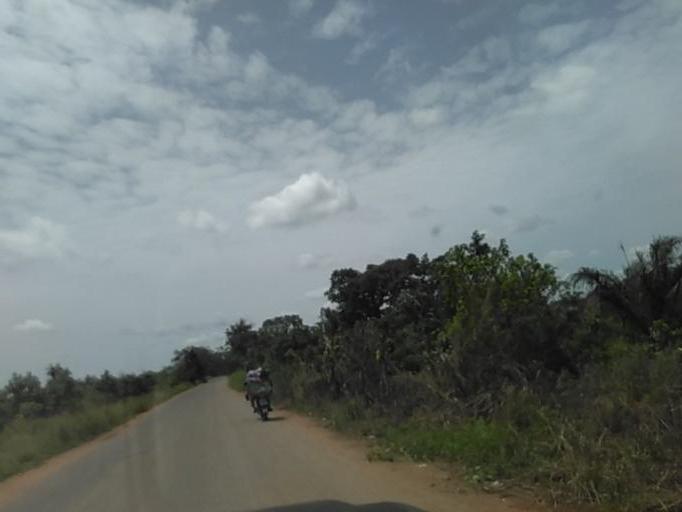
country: GH
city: Akropong
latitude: 6.0937
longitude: 0.1737
